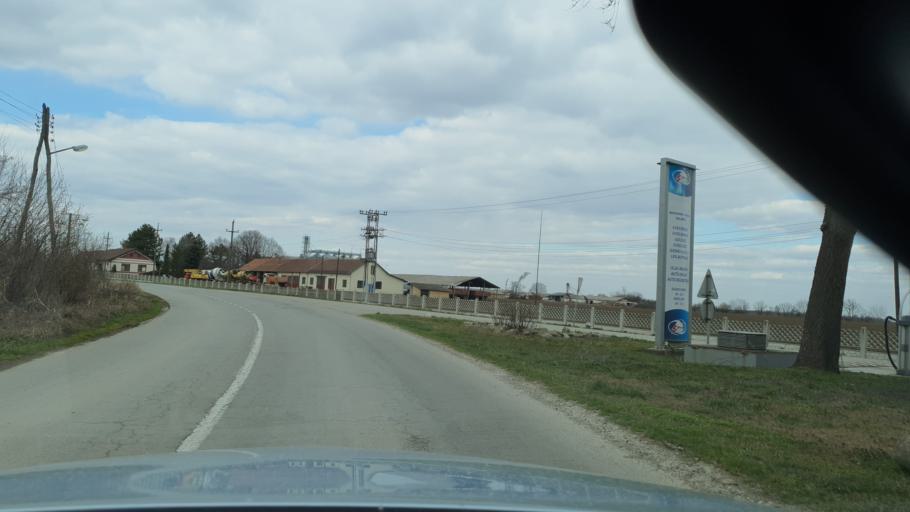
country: RS
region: Autonomna Pokrajina Vojvodina
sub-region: Juznobacki Okrug
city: Bac
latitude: 45.4154
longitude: 19.3142
